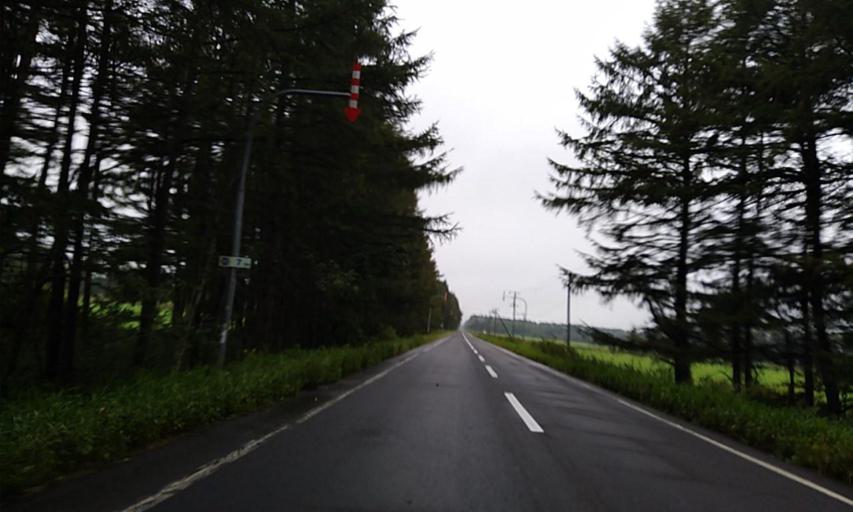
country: JP
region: Hokkaido
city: Shibetsu
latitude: 43.5010
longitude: 144.6557
